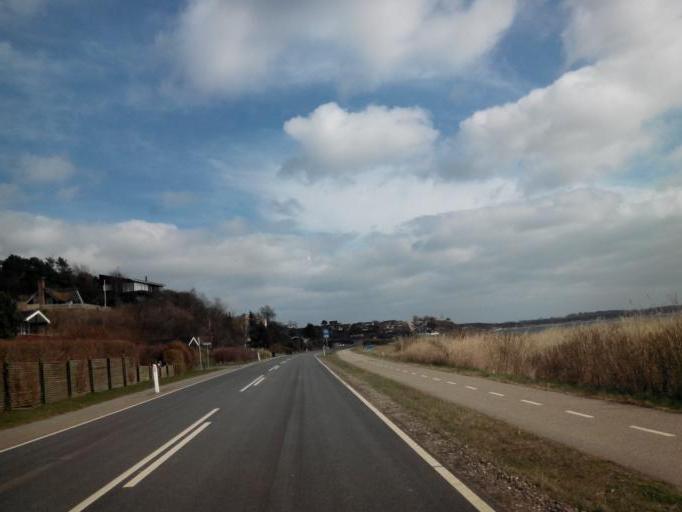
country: DK
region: Central Jutland
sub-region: Syddjurs Kommune
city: Ebeltoft
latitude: 56.2270
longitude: 10.6342
